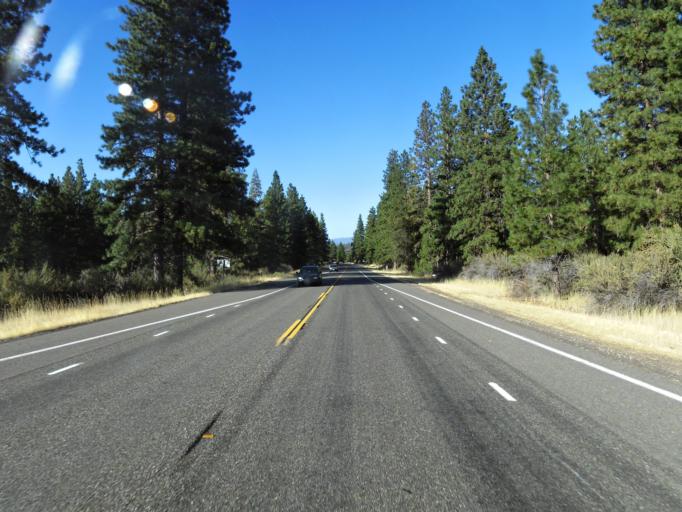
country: US
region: California
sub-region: Siskiyou County
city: Weed
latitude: 41.4548
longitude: -122.3593
